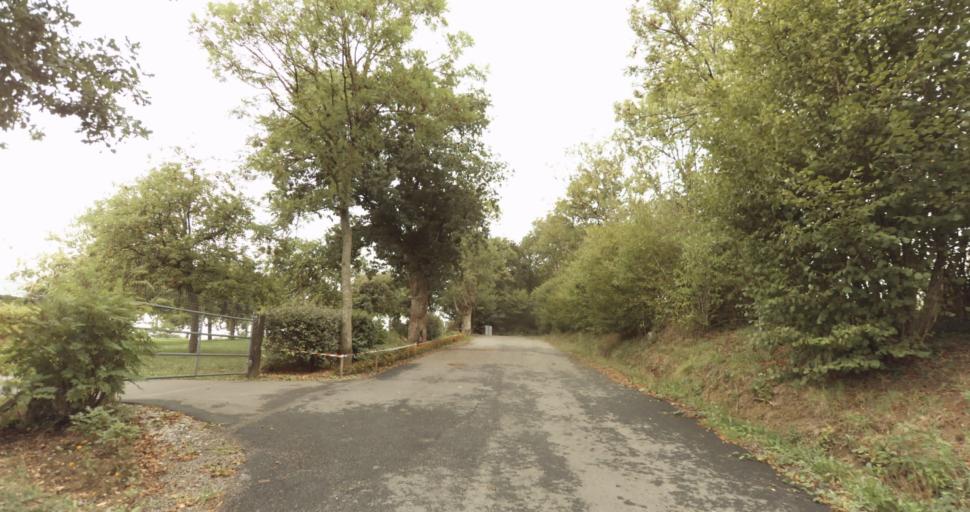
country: FR
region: Lower Normandy
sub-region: Departement de l'Orne
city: Gace
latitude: 48.7132
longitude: 0.3297
